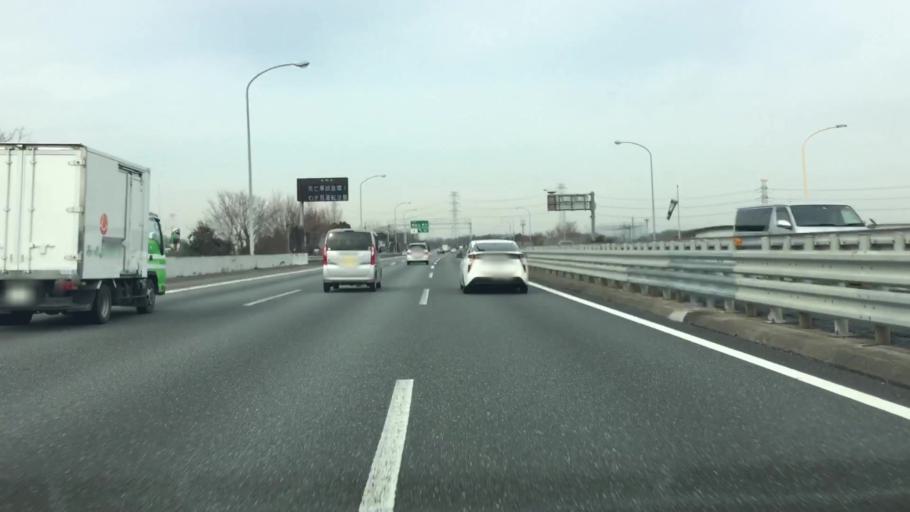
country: JP
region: Saitama
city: Sakado
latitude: 36.0207
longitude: 139.3823
